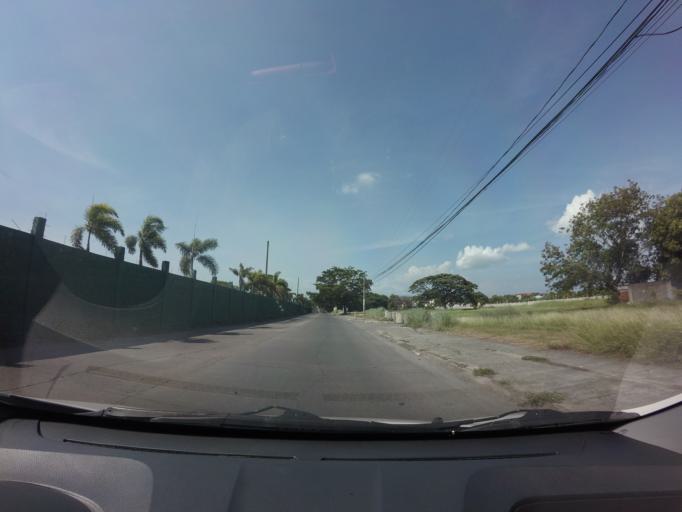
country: PH
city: Sambayanihan People's Village
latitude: 14.4420
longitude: 121.0068
